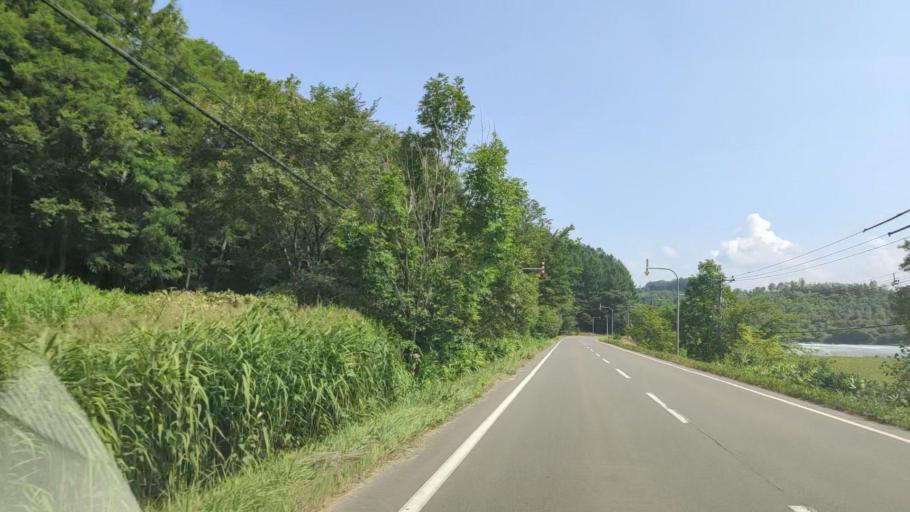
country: JP
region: Hokkaido
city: Shimo-furano
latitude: 43.4292
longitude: 142.4069
